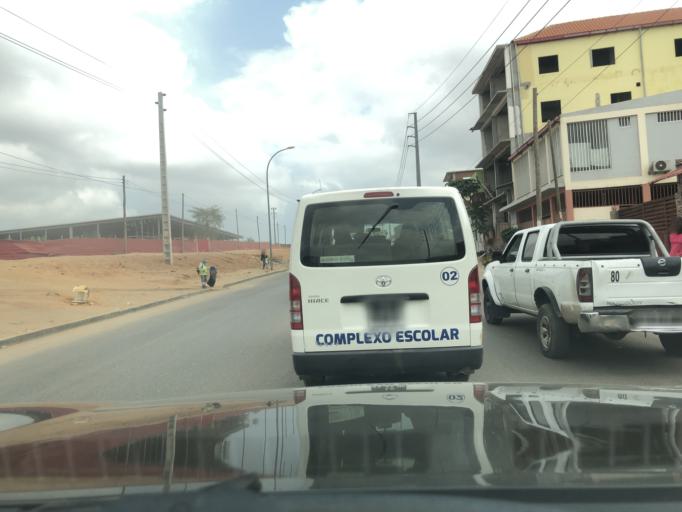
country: AO
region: Luanda
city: Luanda
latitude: -8.9152
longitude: 13.2107
